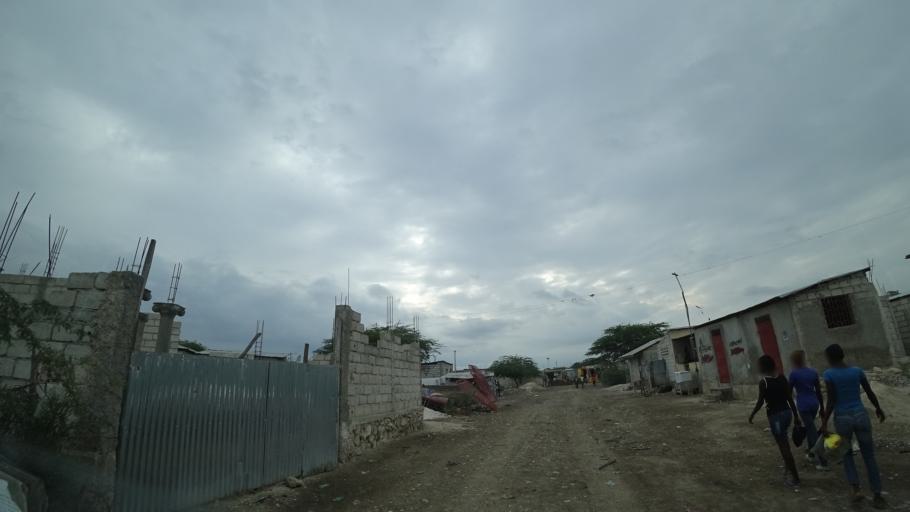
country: HT
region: Ouest
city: Croix des Bouquets
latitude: 18.6457
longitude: -72.2751
